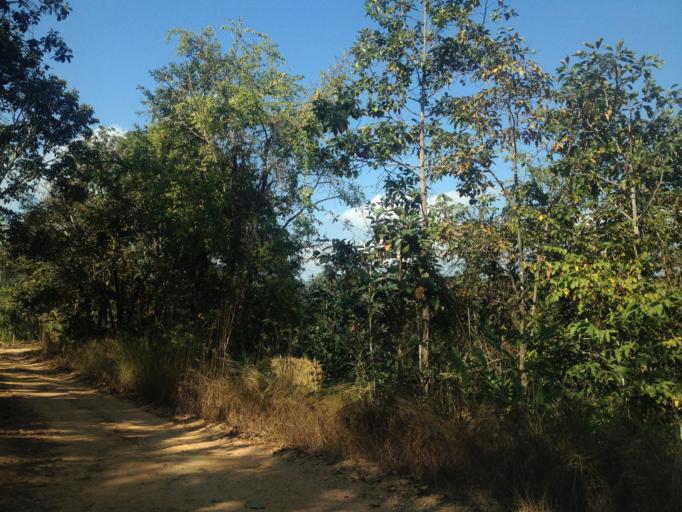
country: TH
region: Mae Hong Son
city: Ban Huai I Huak
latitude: 18.1248
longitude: 98.2009
